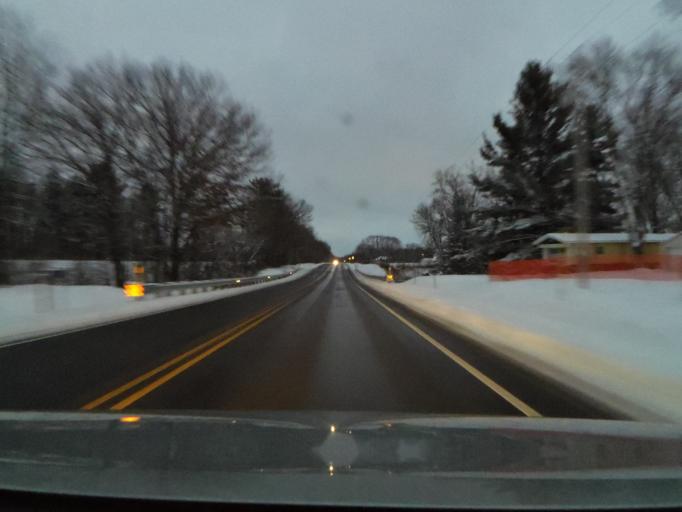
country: US
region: Wisconsin
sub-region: Dunn County
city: Menomonie
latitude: 44.9237
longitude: -91.9716
